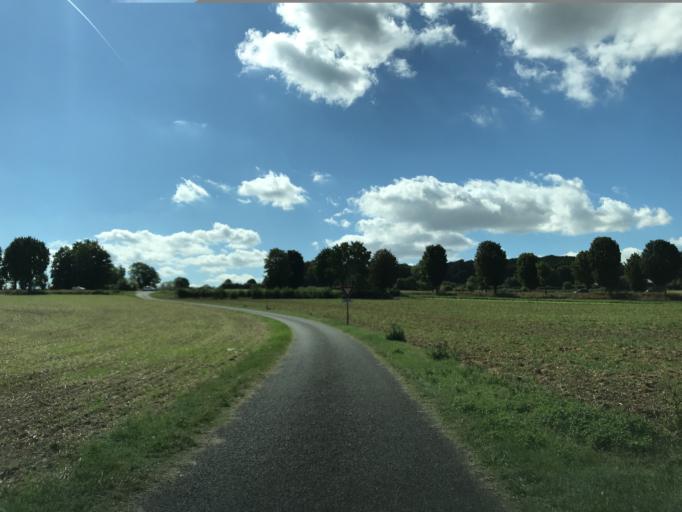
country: FR
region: Haute-Normandie
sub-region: Departement de l'Eure
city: Saint-Just
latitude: 49.1466
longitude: 1.4049
